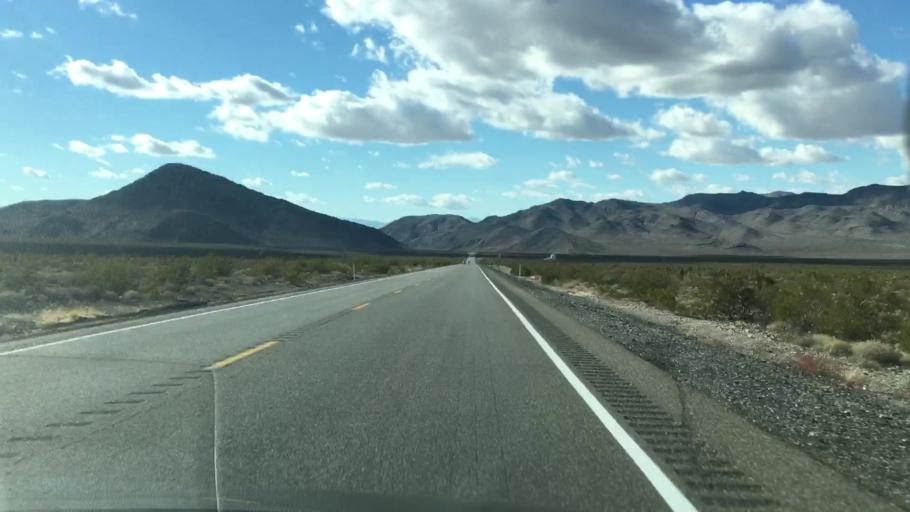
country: US
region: Nevada
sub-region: Nye County
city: Pahrump
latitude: 36.5933
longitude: -116.0246
